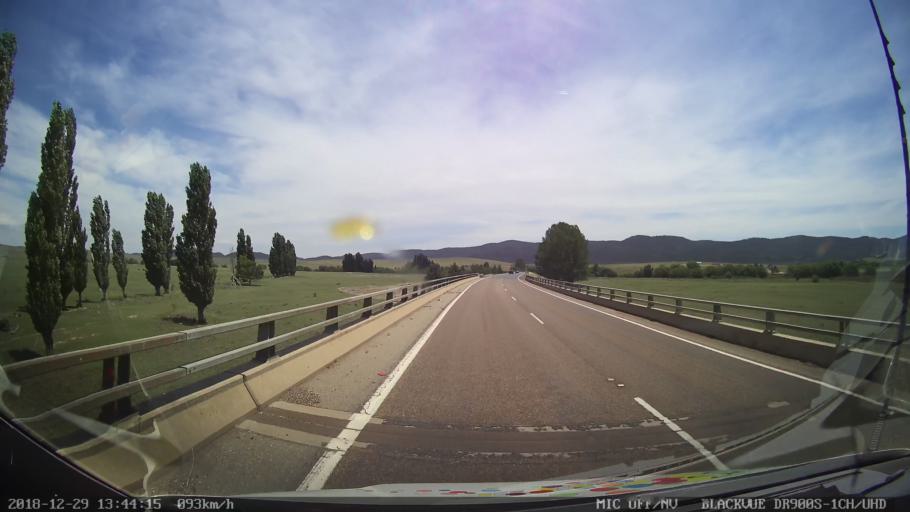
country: AU
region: New South Wales
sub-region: Cooma-Monaro
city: Cooma
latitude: -36.0826
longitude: 149.1552
